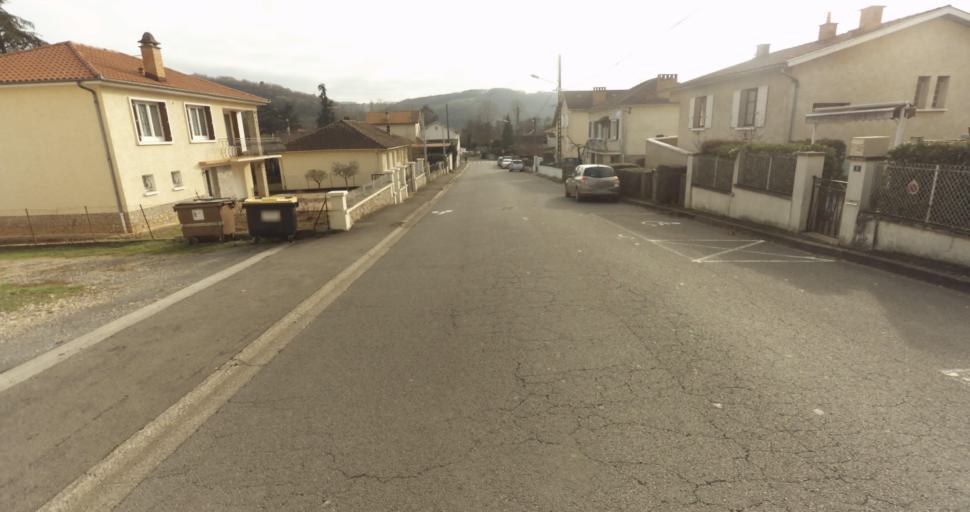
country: FR
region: Midi-Pyrenees
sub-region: Departement du Lot
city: Figeac
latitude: 44.6103
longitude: 2.0172
